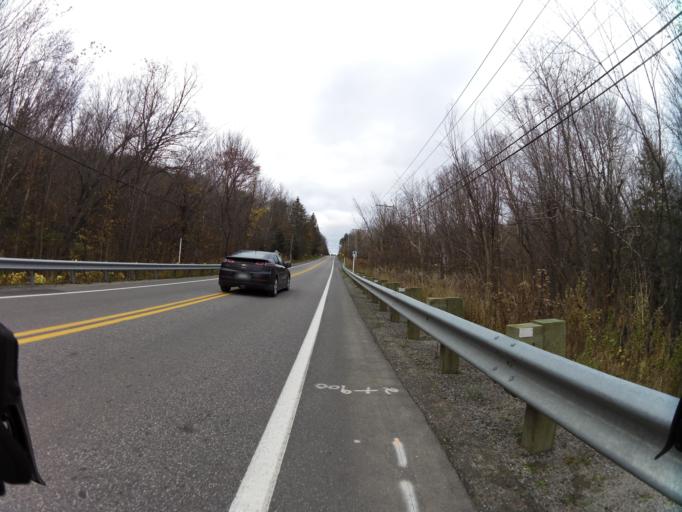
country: CA
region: Quebec
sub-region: Outaouais
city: Wakefield
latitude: 45.5606
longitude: -75.8402
